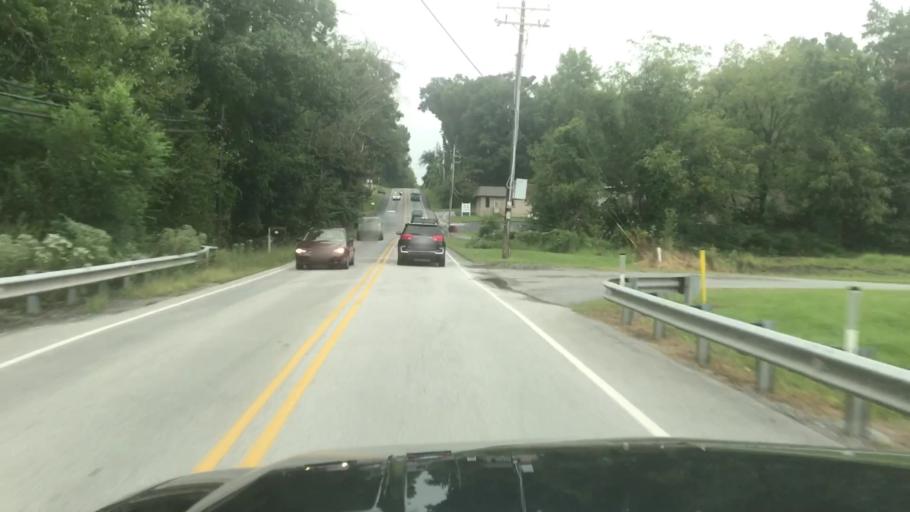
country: US
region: Pennsylvania
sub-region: York County
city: Valley Green
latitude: 40.1693
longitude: -76.8249
